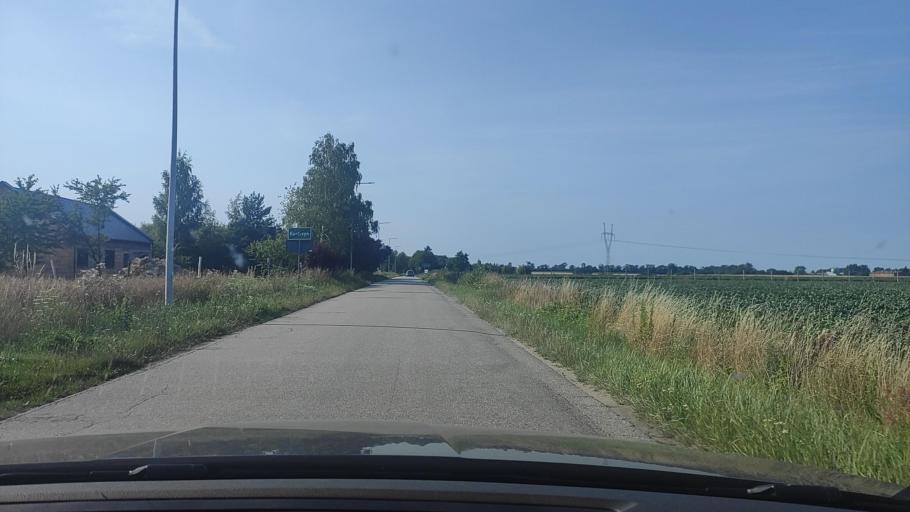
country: PL
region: Greater Poland Voivodeship
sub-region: Powiat poznanski
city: Kostrzyn
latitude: 52.4063
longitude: 17.2198
